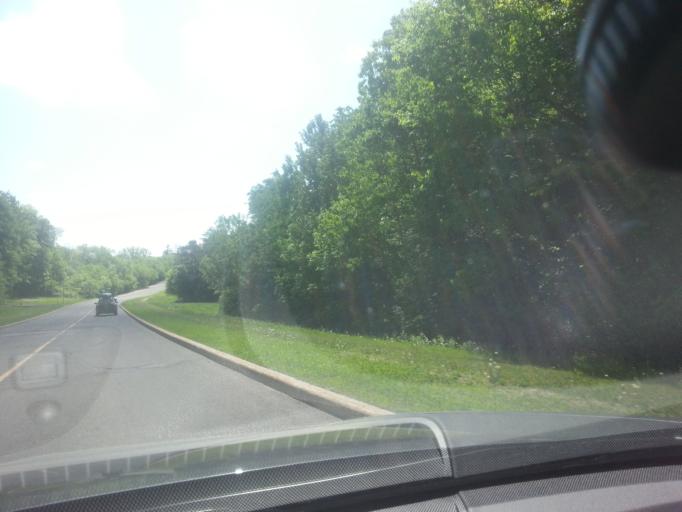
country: CA
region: Ontario
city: Ottawa
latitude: 45.4380
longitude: -75.7581
